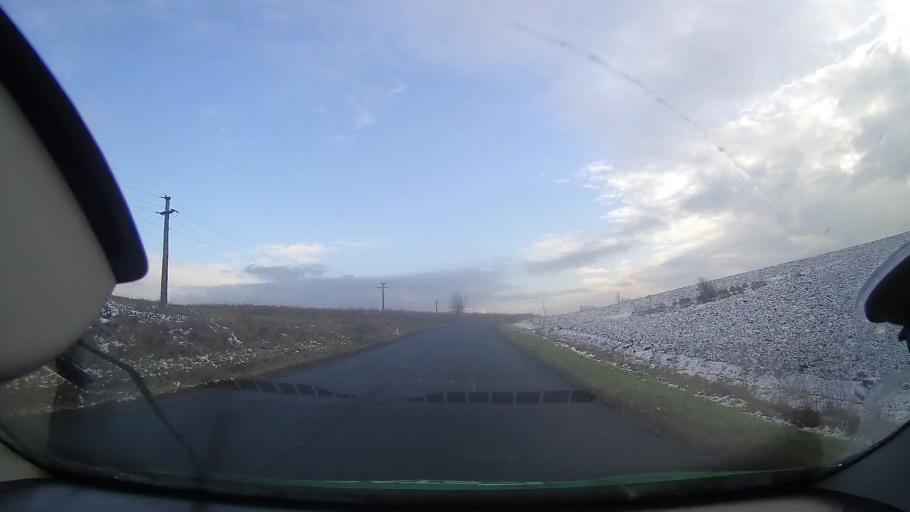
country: RO
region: Mures
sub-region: Comuna Cucerdea
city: Cucerdea
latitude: 46.4183
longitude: 24.2610
